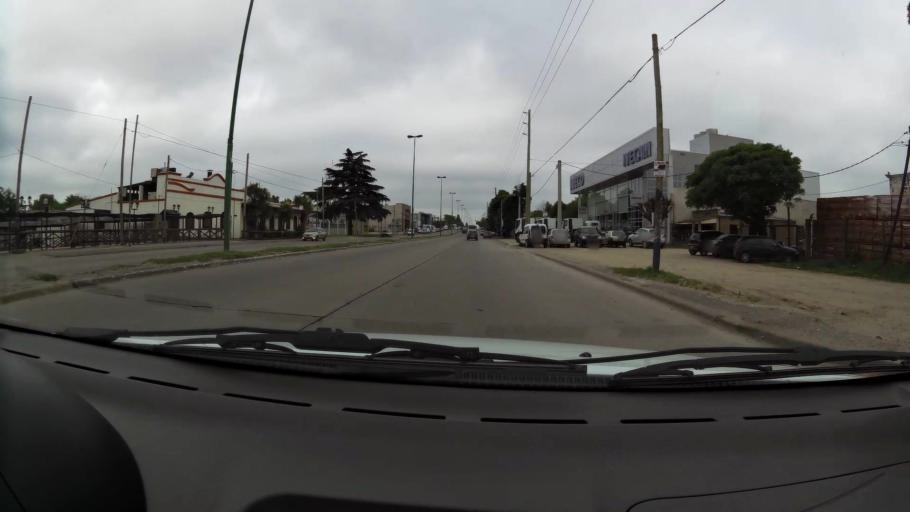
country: AR
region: Buenos Aires
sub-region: Partido de La Plata
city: La Plata
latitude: -34.9523
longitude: -58.0007
